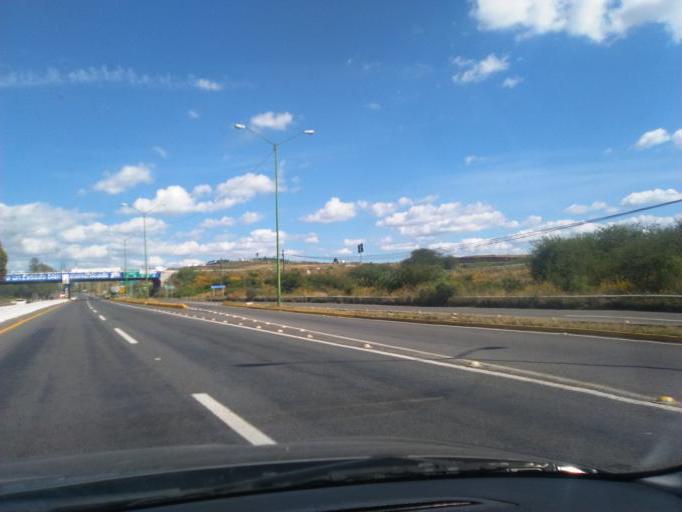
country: MX
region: Guanajuato
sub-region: Silao de la Victoria
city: Aguas Buenas
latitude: 20.9544
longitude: -101.3747
